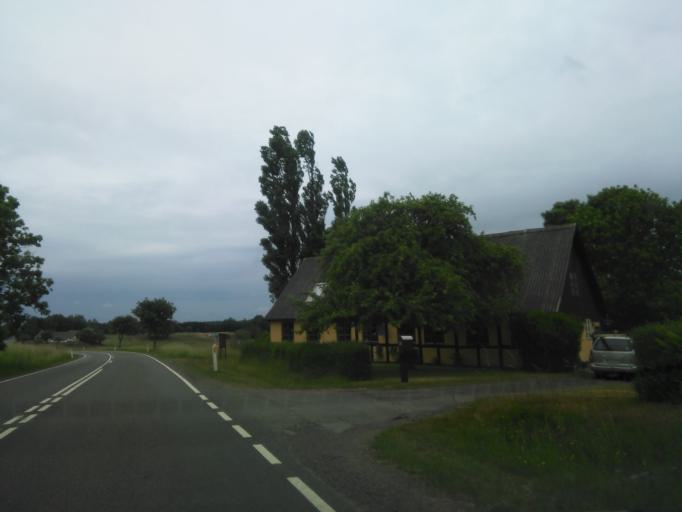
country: DK
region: Capital Region
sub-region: Bornholm Kommune
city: Akirkeby
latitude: 55.0900
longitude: 14.8760
